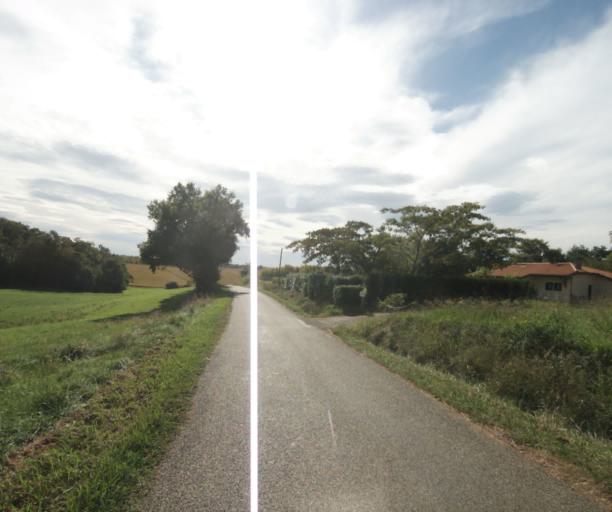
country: FR
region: Midi-Pyrenees
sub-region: Departement du Gers
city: Cazaubon
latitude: 43.9019
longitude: -0.1579
